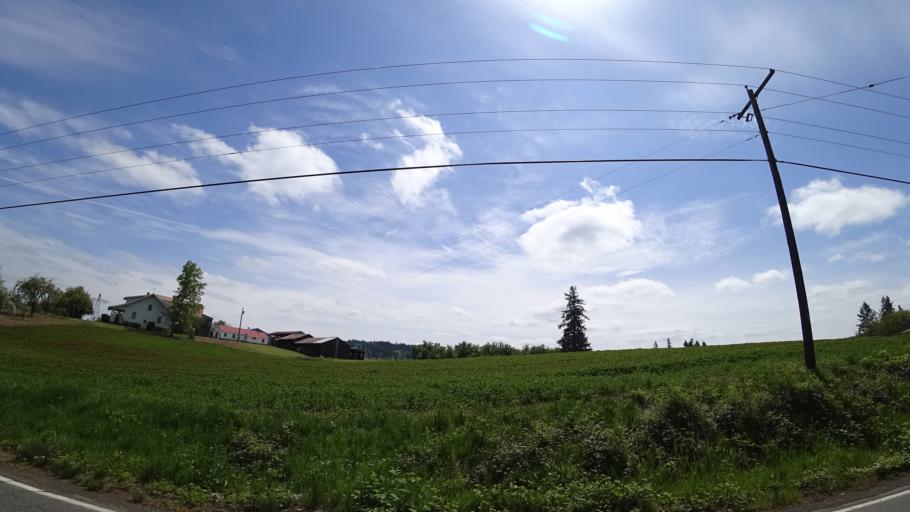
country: US
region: Oregon
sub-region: Washington County
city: Aloha
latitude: 45.4699
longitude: -122.9077
